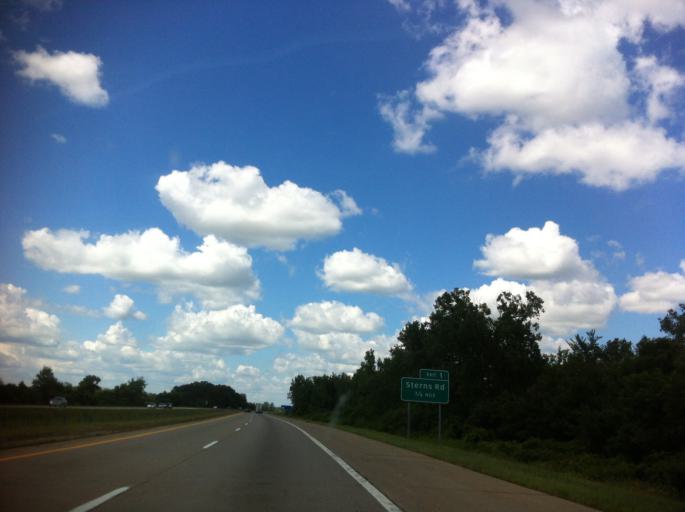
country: US
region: Ohio
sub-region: Lucas County
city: Sylvania
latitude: 41.7341
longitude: -83.6900
